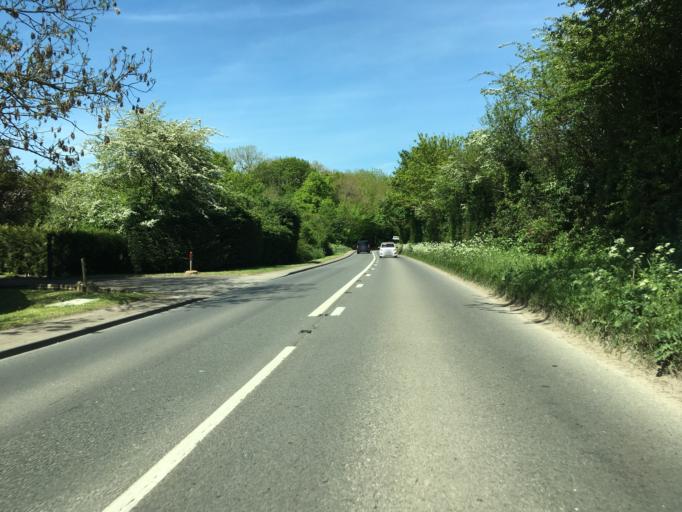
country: GB
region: England
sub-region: Wiltshire
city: Malmesbury
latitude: 51.5727
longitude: -2.0974
